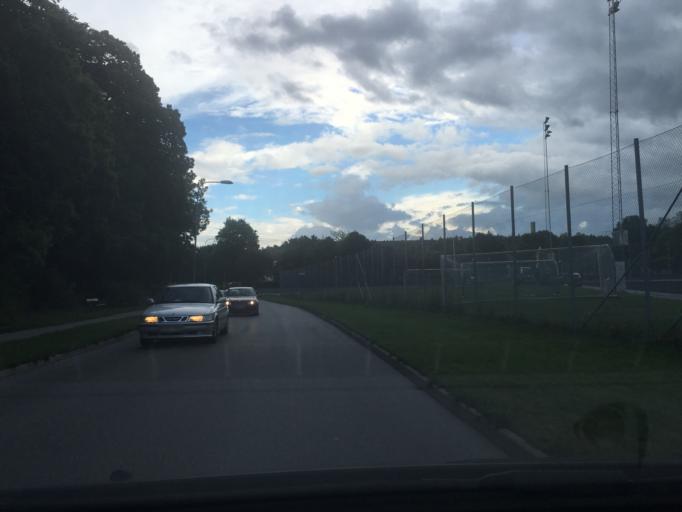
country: SE
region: Stockholm
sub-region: Stockholms Kommun
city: Bromma
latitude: 59.3379
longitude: 17.9269
